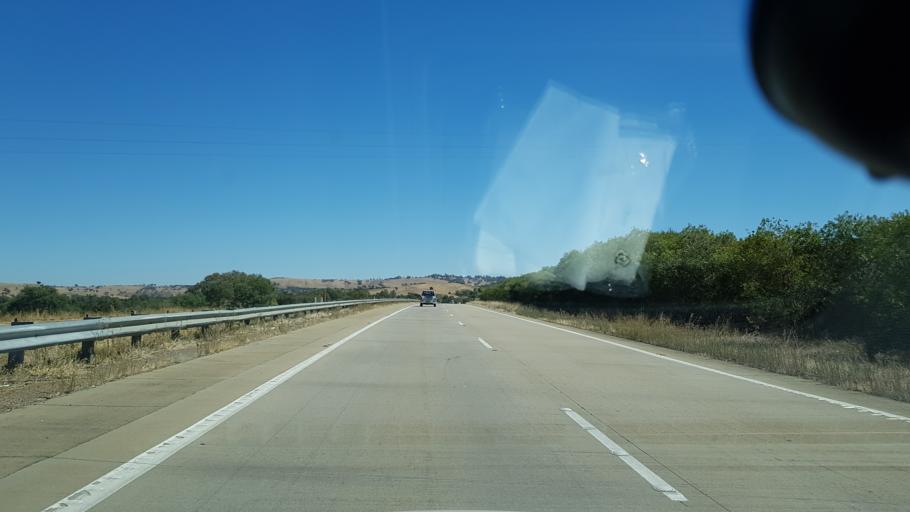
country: AU
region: New South Wales
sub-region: Gundagai
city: Gundagai
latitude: -34.8199
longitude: 148.3677
